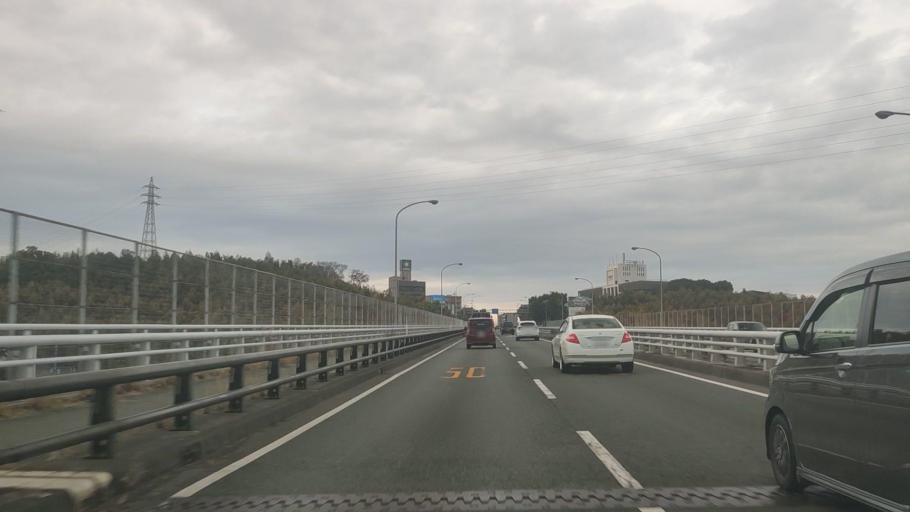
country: JP
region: Kumamoto
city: Ozu
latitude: 32.8481
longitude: 130.7821
